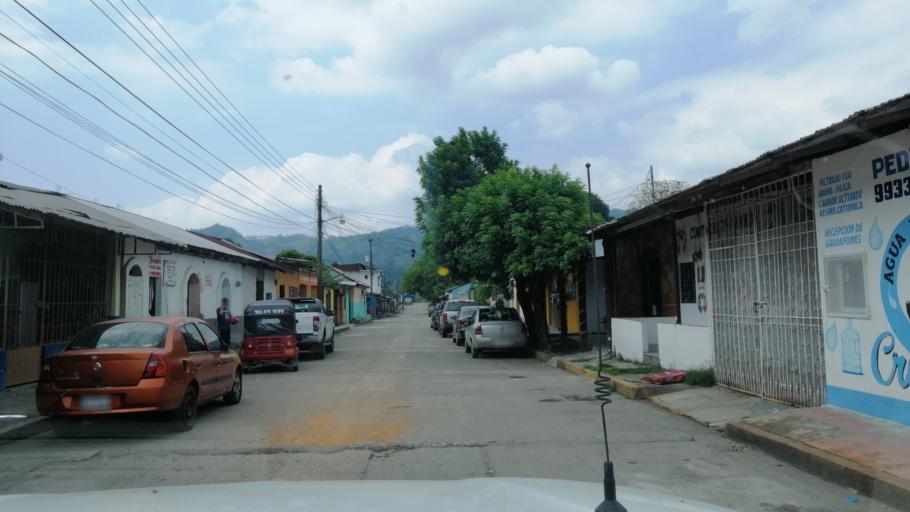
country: MX
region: Chiapas
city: Ostuacan
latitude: 17.4070
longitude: -93.3373
